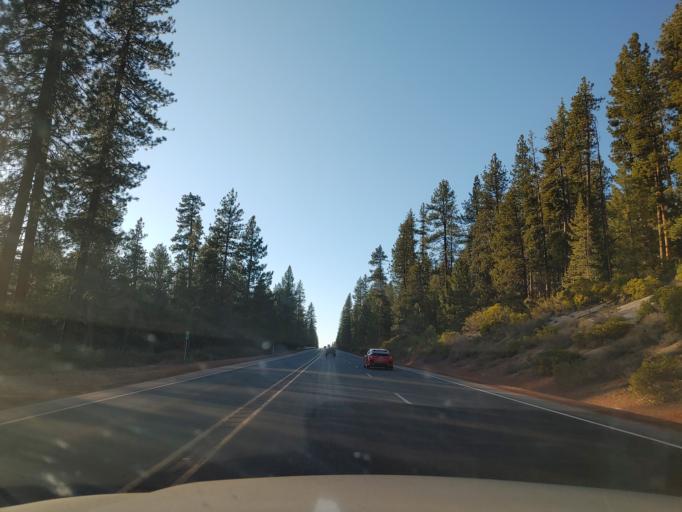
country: US
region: Oregon
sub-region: Deschutes County
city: La Pine
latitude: 43.4515
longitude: -121.8709
